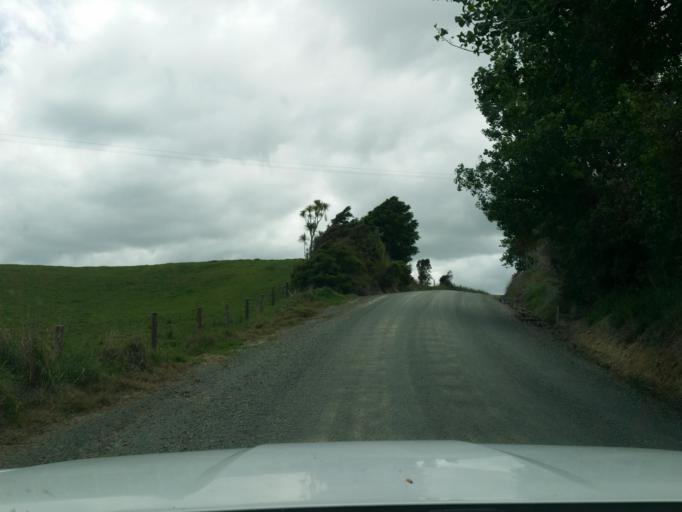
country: NZ
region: Auckland
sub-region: Auckland
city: Wellsford
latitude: -36.2726
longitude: 174.3712
